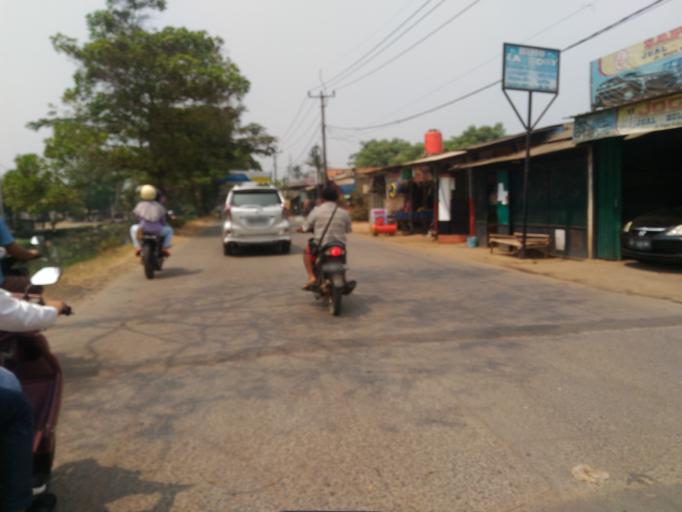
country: ID
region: West Java
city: Pasarkemis
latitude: -6.1443
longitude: 106.5513
